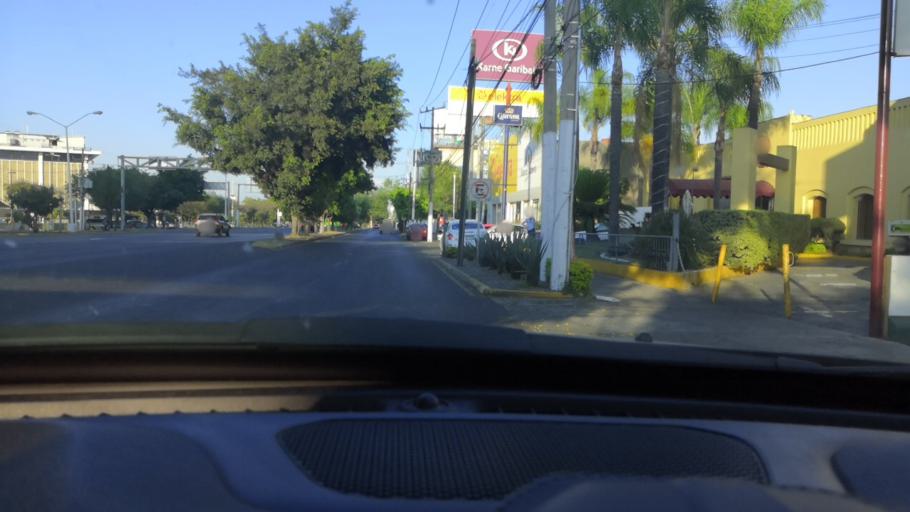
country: MX
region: Jalisco
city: Guadalajara
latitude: 20.6478
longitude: -103.4037
